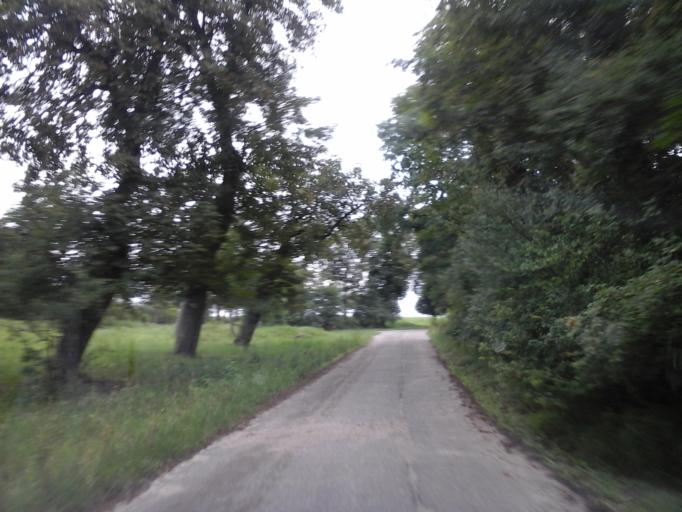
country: PL
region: West Pomeranian Voivodeship
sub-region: Powiat choszczenski
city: Krzecin
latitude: 52.9737
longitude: 15.4262
